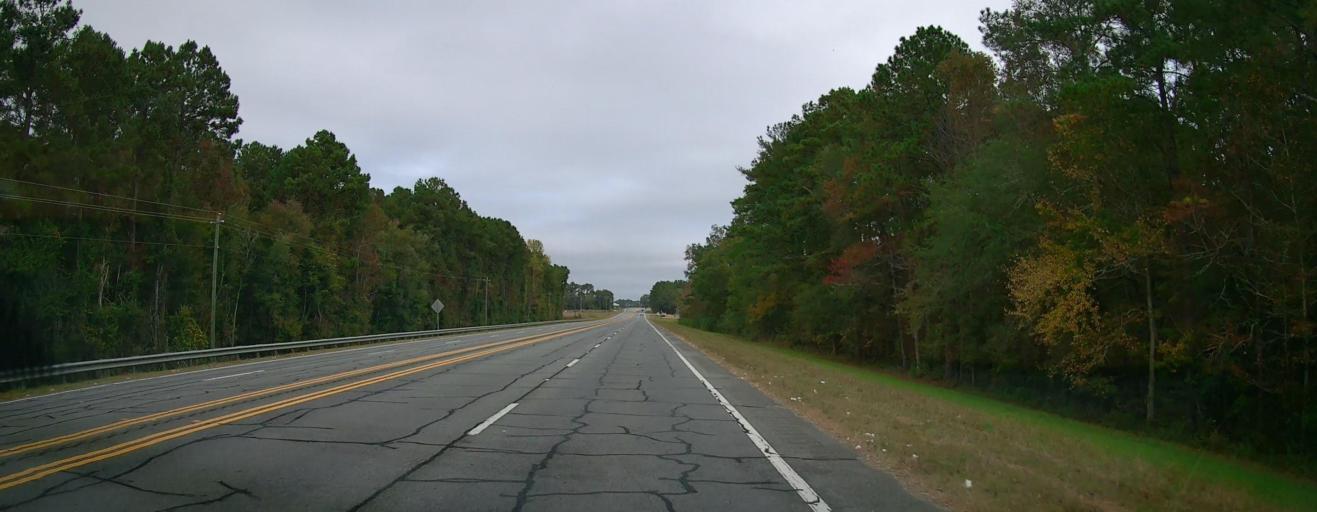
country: US
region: Georgia
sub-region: Tift County
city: Omega
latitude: 31.3237
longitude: -83.6215
